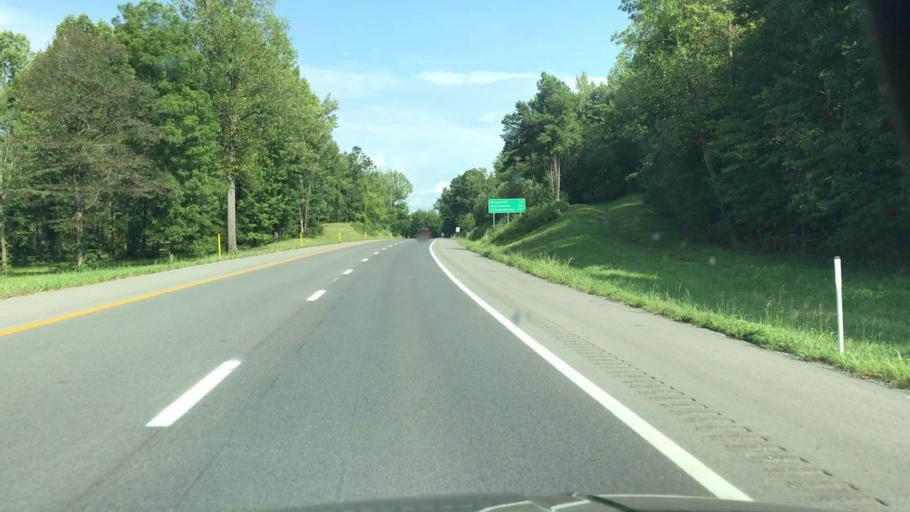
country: US
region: Kentucky
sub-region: Hopkins County
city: Nortonville
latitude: 37.2119
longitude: -87.4260
